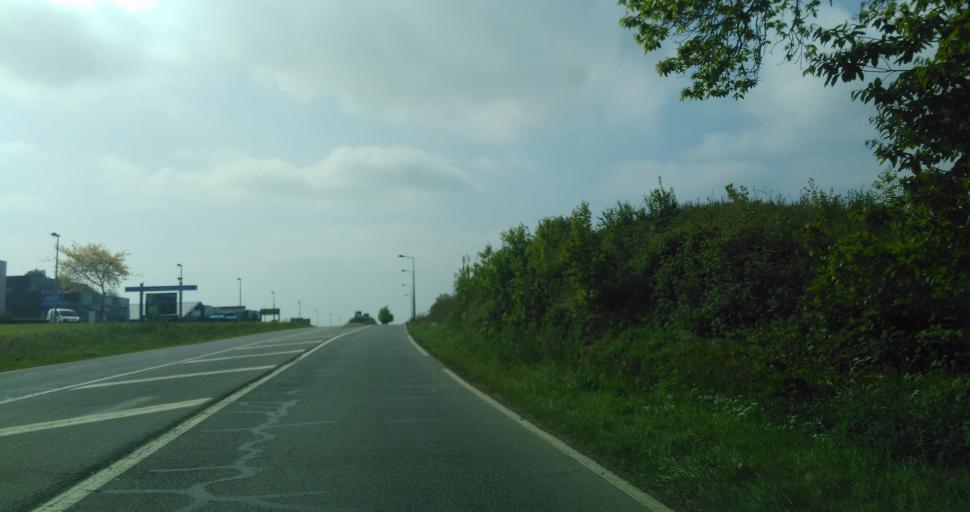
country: FR
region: Brittany
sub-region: Departement d'Ille-et-Vilaine
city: La Chapelle-des-Fougeretz
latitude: 48.1852
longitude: -1.7253
